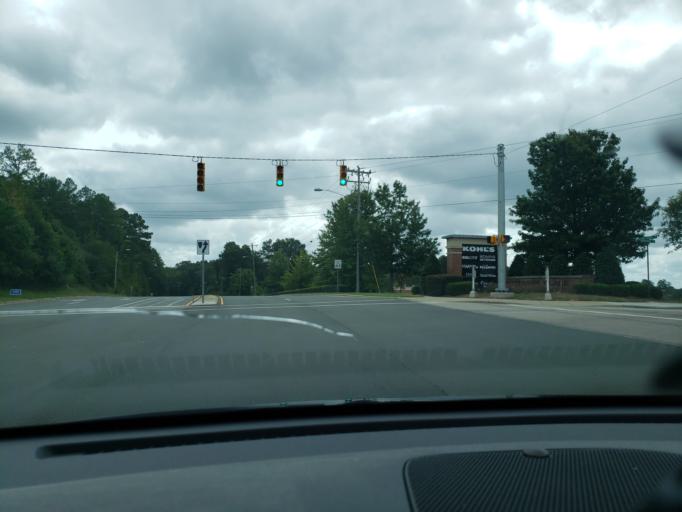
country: US
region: North Carolina
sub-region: Orange County
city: Chapel Hill
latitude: 35.9532
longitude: -78.9894
